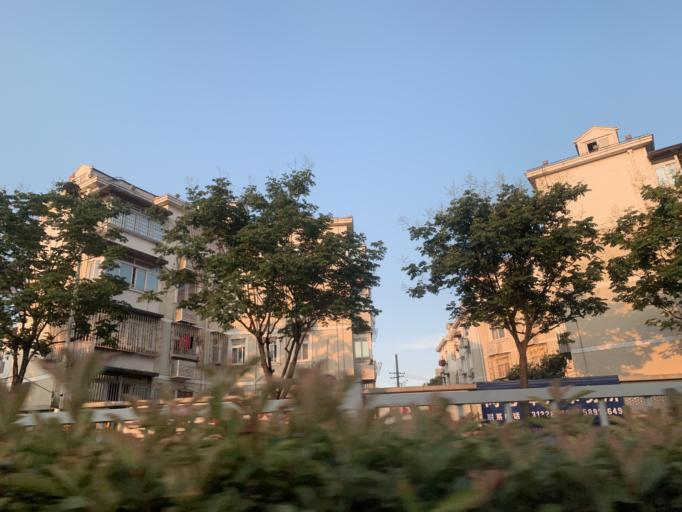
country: CN
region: Shanghai Shi
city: Huamu
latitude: 31.1859
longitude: 121.5502
